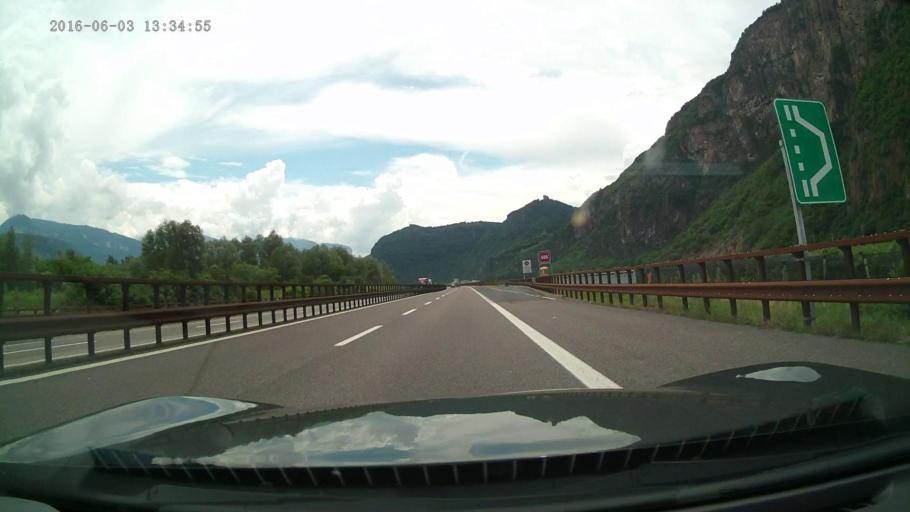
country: IT
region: Trentino-Alto Adige
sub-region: Bolzano
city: Vadena
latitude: 46.3973
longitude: 11.2970
